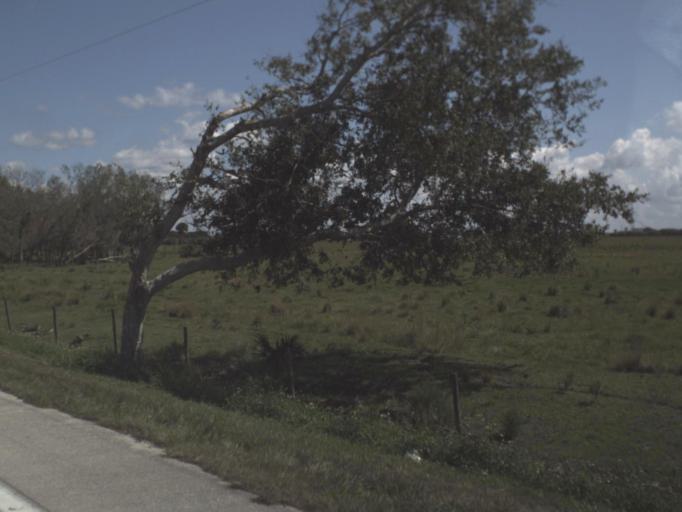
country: US
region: Florida
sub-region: Glades County
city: Buckhead Ridge
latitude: 27.1267
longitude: -80.9097
